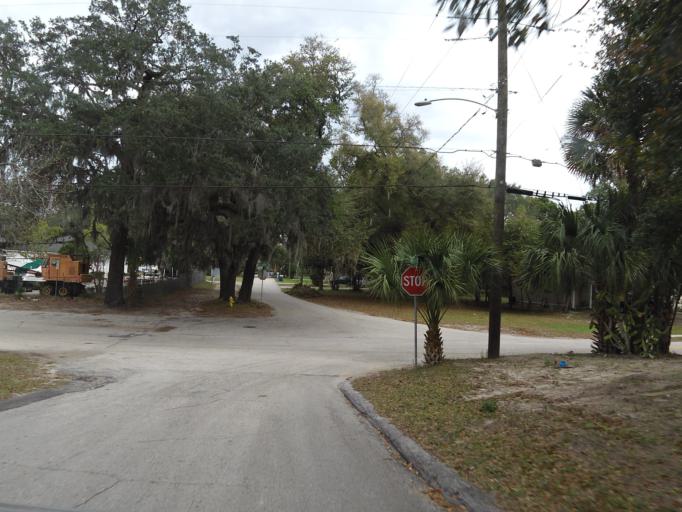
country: US
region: Florida
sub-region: Duval County
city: Jacksonville
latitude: 30.3337
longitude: -81.6106
